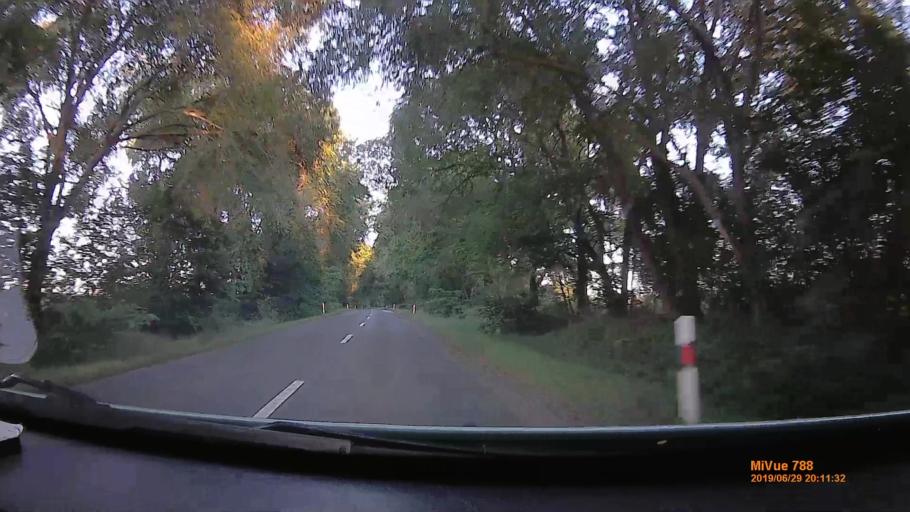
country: HU
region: Pest
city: Paty
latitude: 47.5263
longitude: 18.7934
